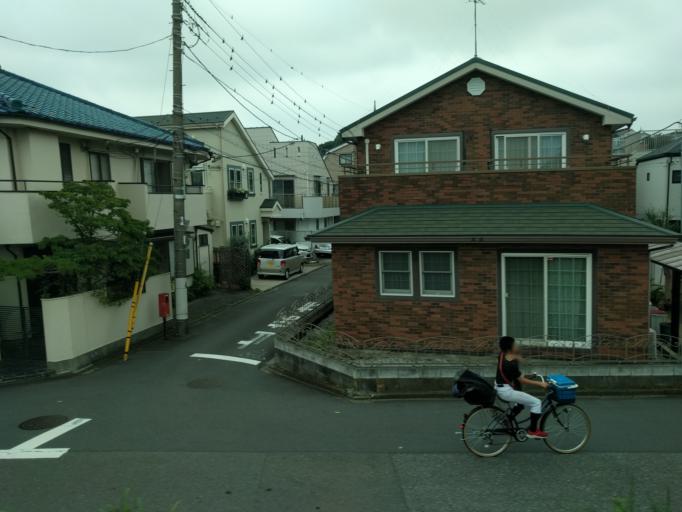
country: JP
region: Kanagawa
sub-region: Kawasaki-shi
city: Kawasaki
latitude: 35.5921
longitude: 139.6599
